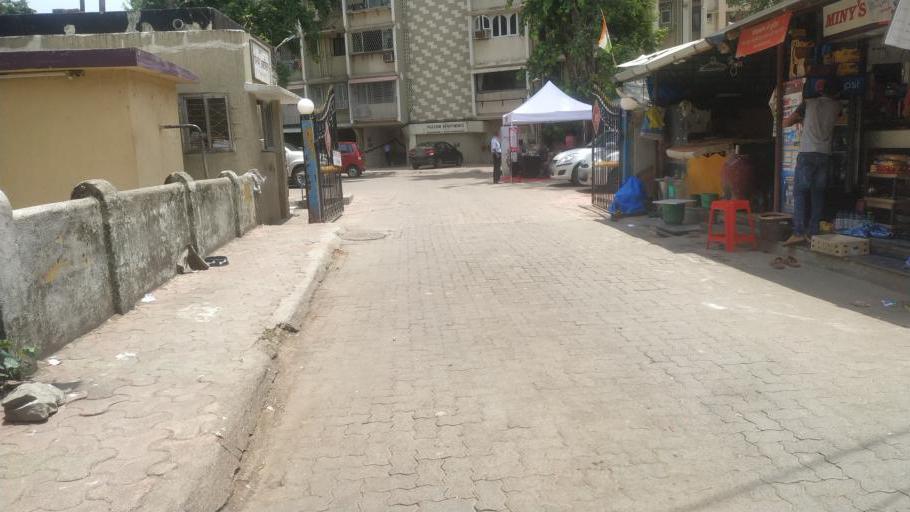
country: IN
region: Maharashtra
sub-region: Mumbai Suburban
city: Mumbai
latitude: 19.0203
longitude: 72.8313
